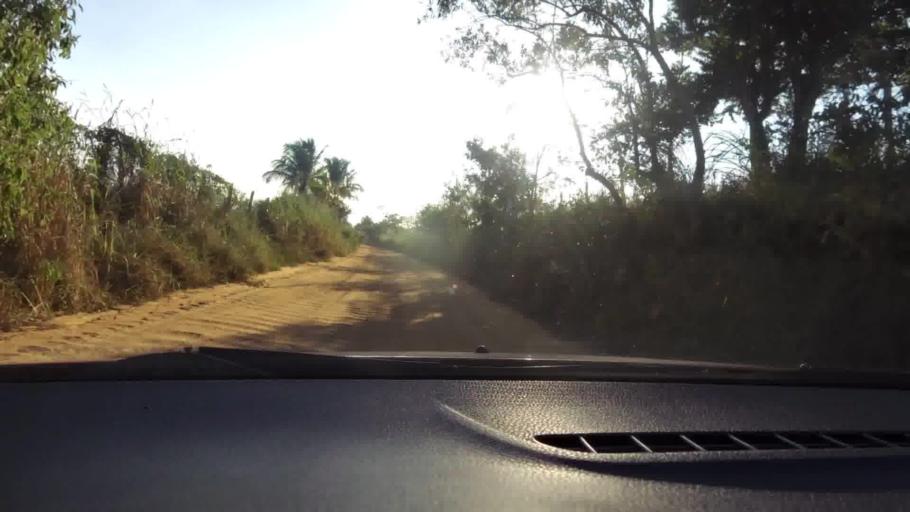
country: BR
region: Espirito Santo
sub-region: Guarapari
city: Guarapari
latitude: -20.5374
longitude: -40.4426
